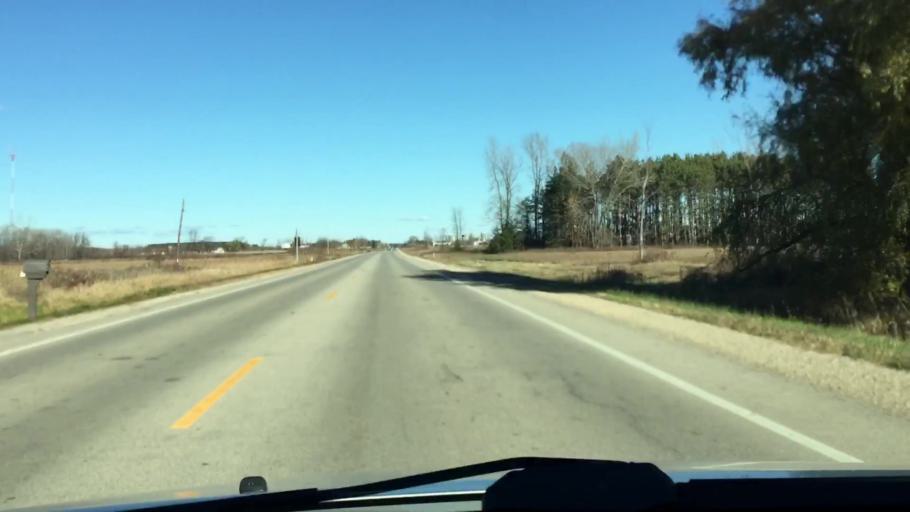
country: US
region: Wisconsin
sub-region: Brown County
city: Pulaski
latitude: 44.7178
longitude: -88.2455
